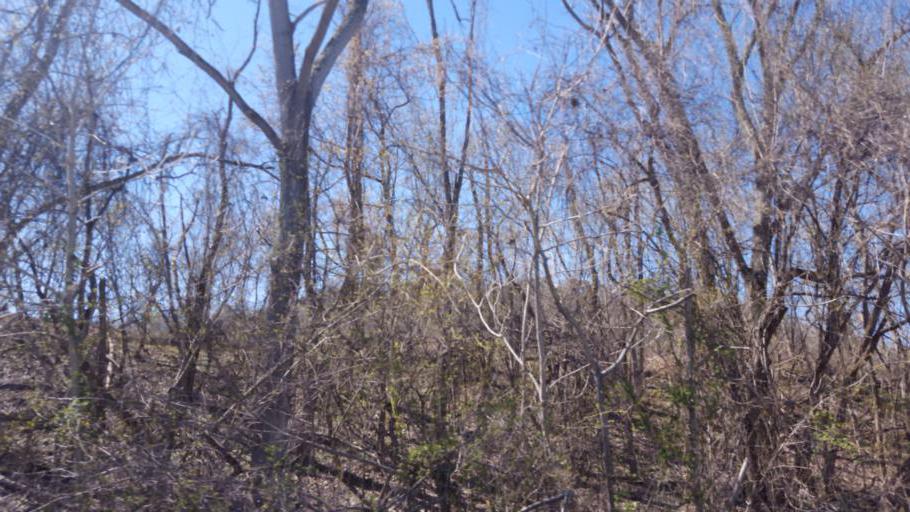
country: US
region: Ohio
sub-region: Belmont County
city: Yorkville
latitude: 40.1518
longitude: -80.7064
